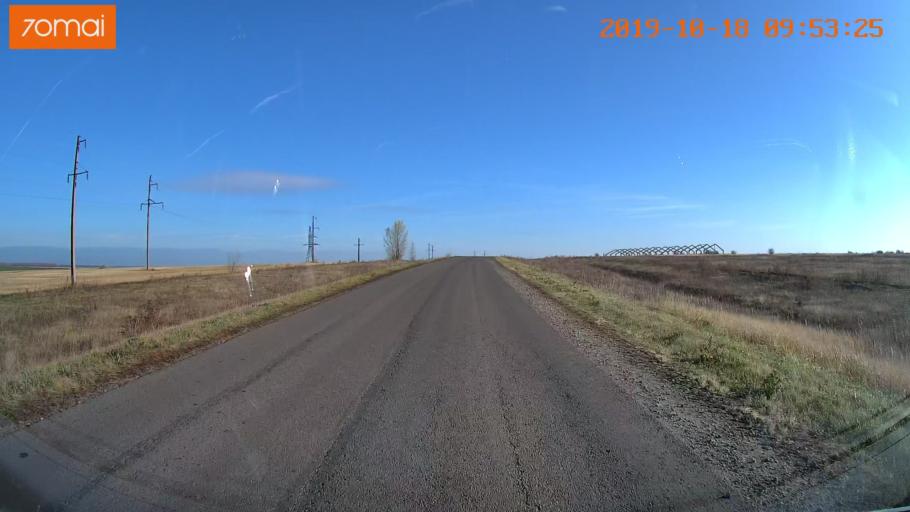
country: RU
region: Tula
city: Kazachka
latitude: 53.3608
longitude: 38.3284
